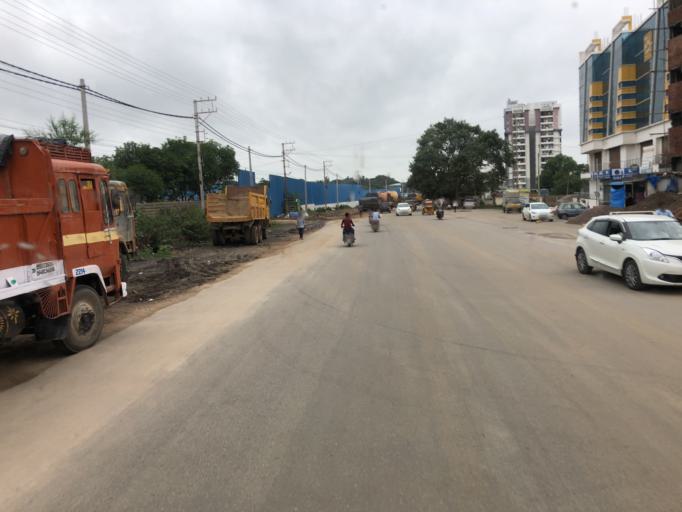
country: IN
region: Telangana
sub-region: Medak
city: Serilingampalle
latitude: 17.4662
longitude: 78.3389
